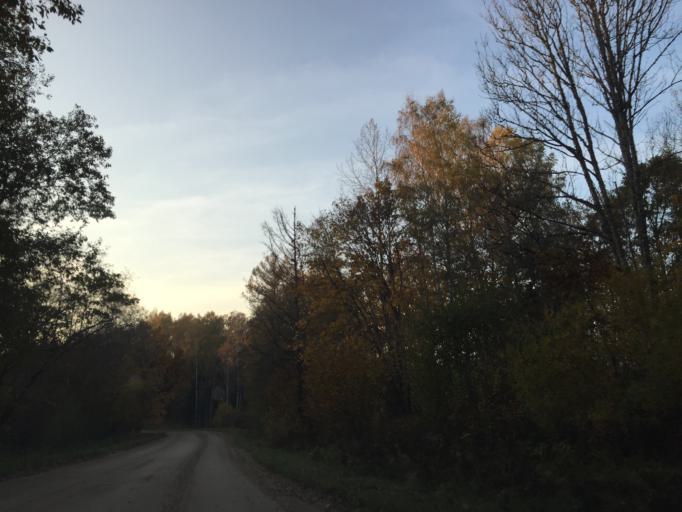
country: LV
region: Priekule
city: Priekule
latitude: 56.4800
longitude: 21.7193
